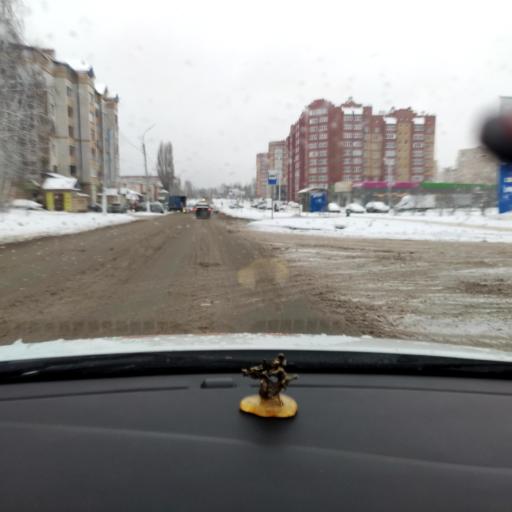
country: RU
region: Tatarstan
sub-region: Zelenodol'skiy Rayon
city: Zelenodolsk
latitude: 55.8575
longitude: 48.5589
